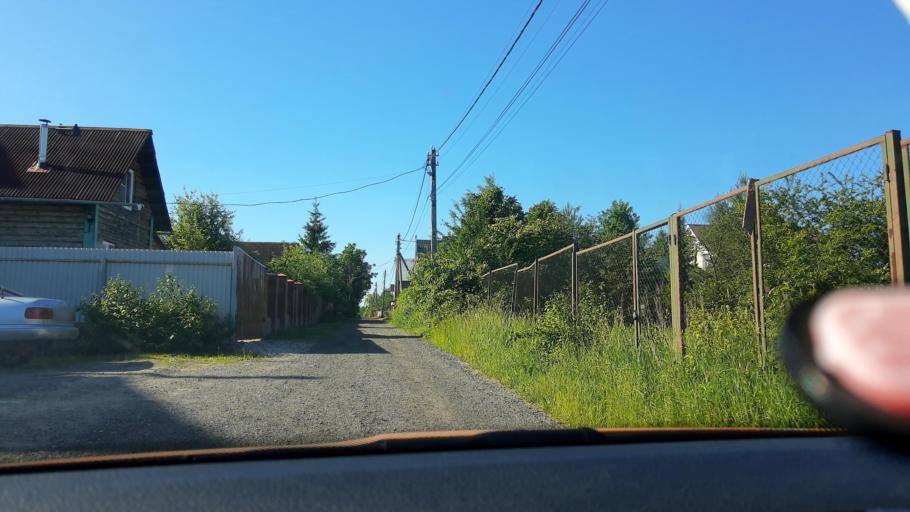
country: RU
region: Moskovskaya
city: Kommunarka
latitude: 55.5253
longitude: 37.4997
